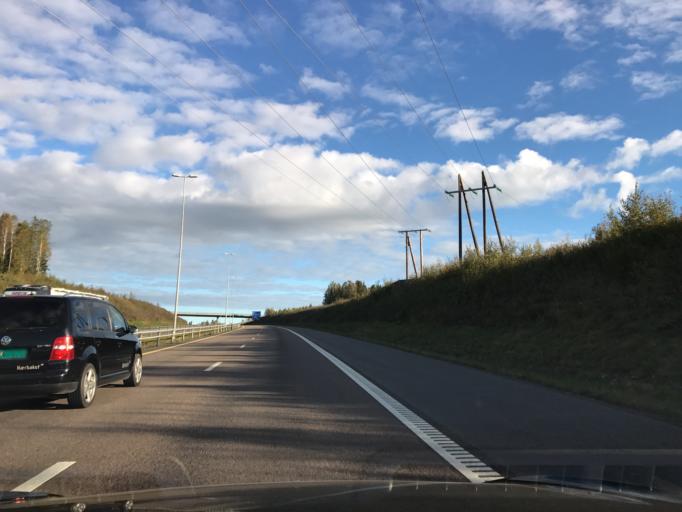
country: NO
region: Akershus
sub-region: Eidsvoll
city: Raholt
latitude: 60.2433
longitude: 11.1816
